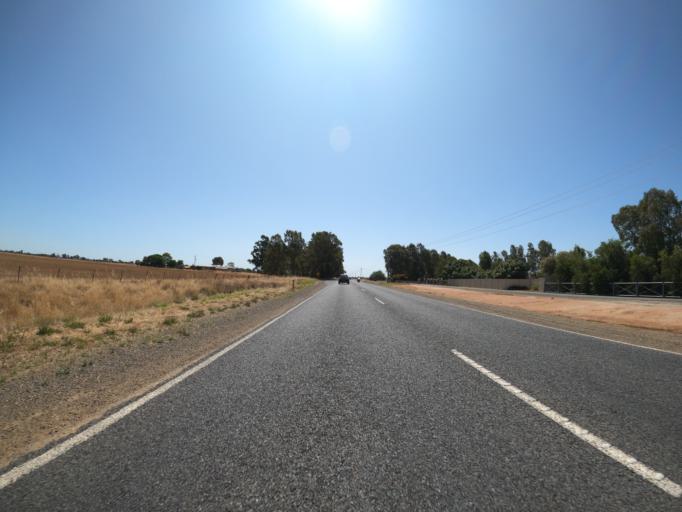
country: AU
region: Victoria
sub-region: Moira
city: Yarrawonga
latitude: -36.0263
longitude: 146.0693
